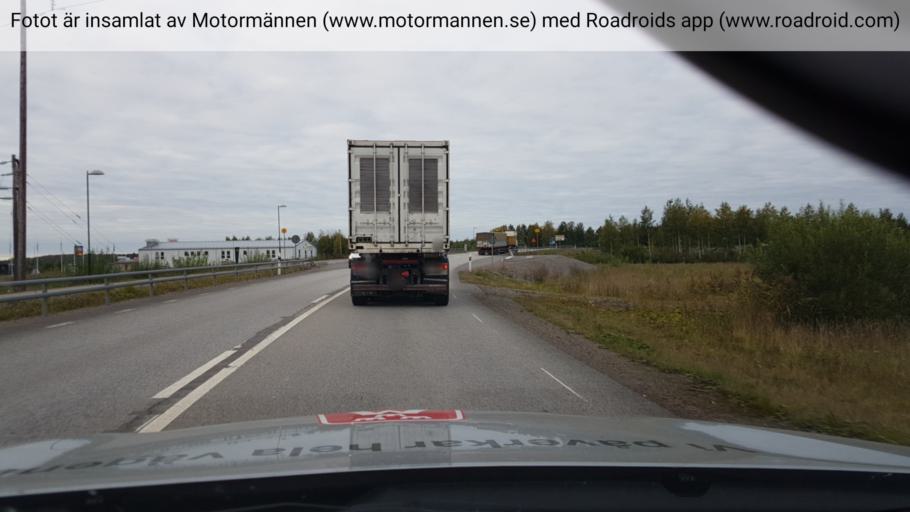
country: SE
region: Uppsala
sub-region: Tierps Kommun
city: Tierp
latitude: 60.3423
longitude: 17.4881
